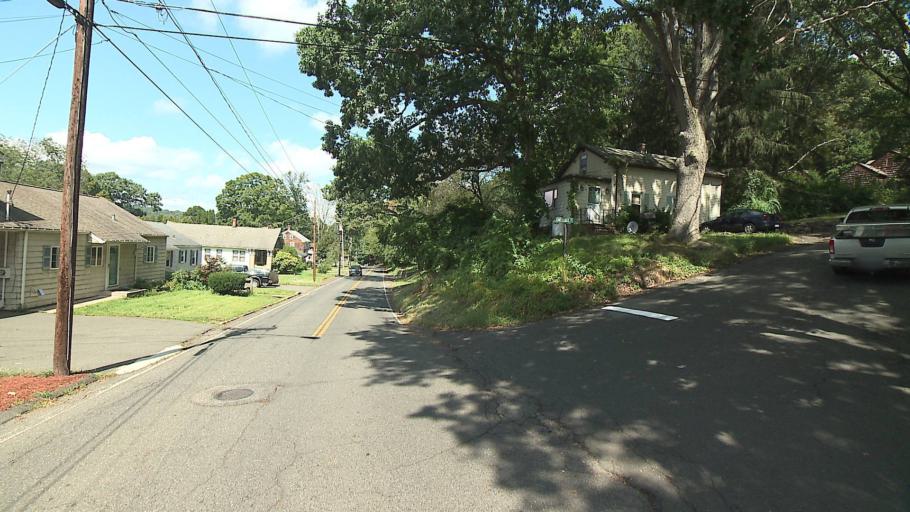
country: US
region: Connecticut
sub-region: New Haven County
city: Seymour
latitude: 41.4001
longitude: -73.0633
